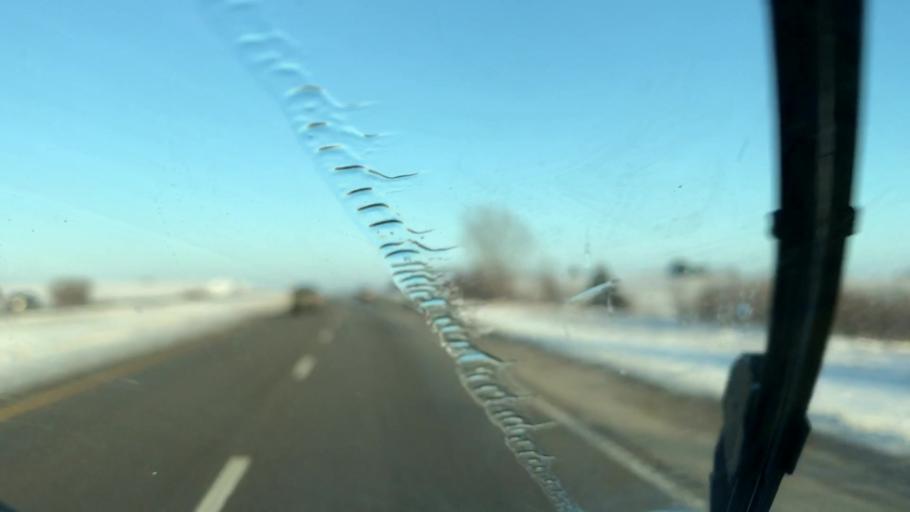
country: US
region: Missouri
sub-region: Andrew County
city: Country Club Village
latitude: 39.7475
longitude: -94.6905
